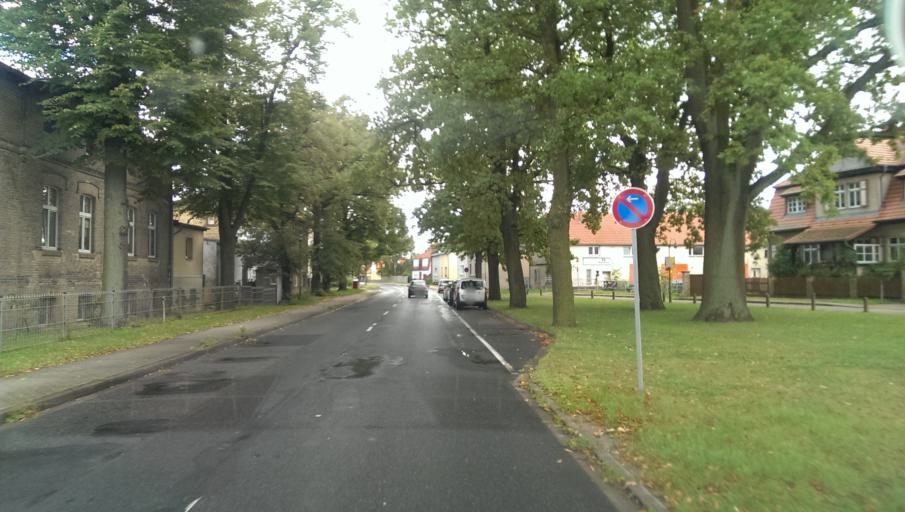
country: DE
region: Brandenburg
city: Velten
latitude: 52.6951
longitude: 13.1123
